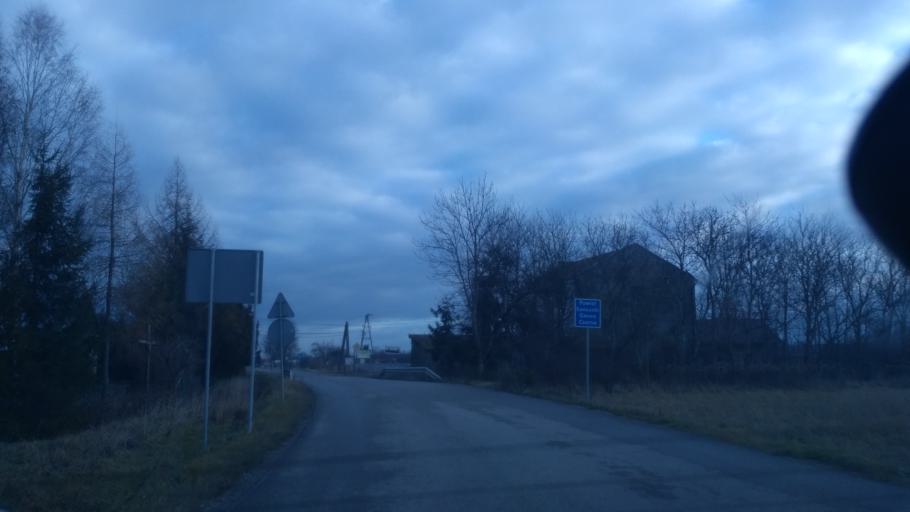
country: PL
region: Subcarpathian Voivodeship
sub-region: Powiat lancucki
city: Czarna
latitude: 50.0940
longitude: 22.1676
